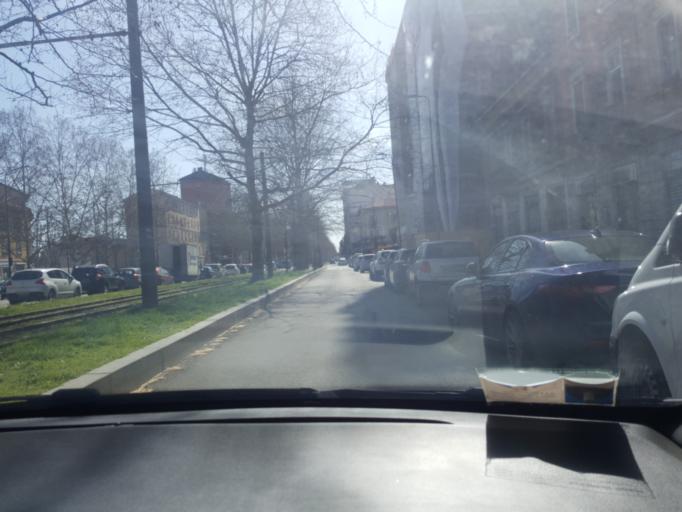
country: IT
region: Lombardy
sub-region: Citta metropolitana di Milano
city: Baranzate
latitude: 45.5030
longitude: 9.1228
